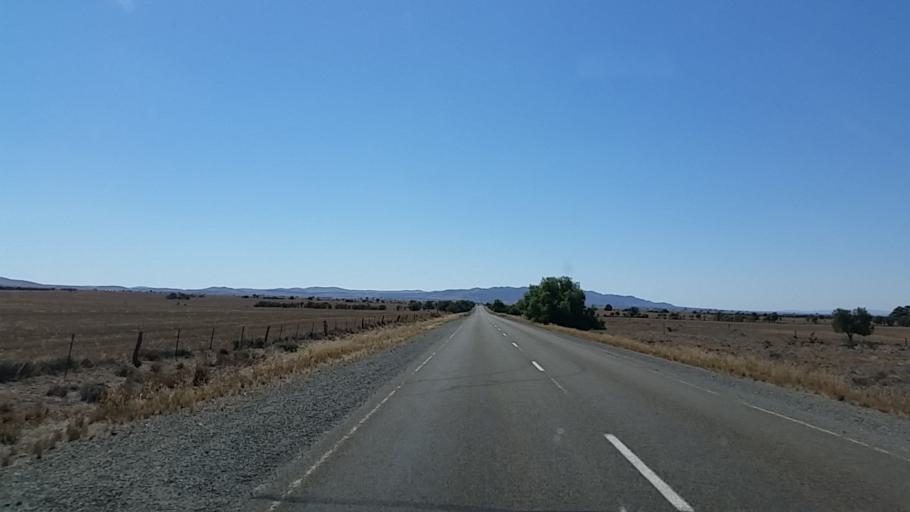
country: AU
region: South Australia
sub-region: Peterborough
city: Peterborough
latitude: -32.6822
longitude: 138.6083
